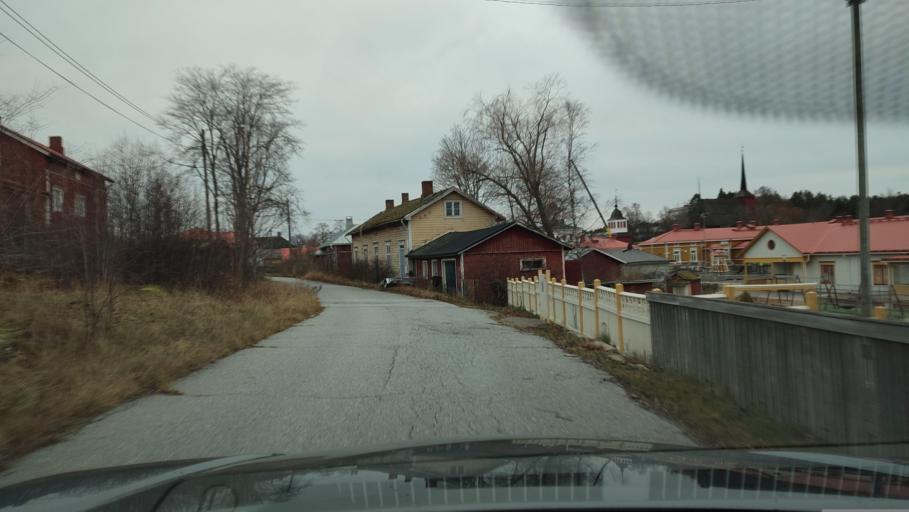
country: FI
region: Ostrobothnia
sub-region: Sydosterbotten
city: Kristinestad
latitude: 62.2769
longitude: 21.3761
